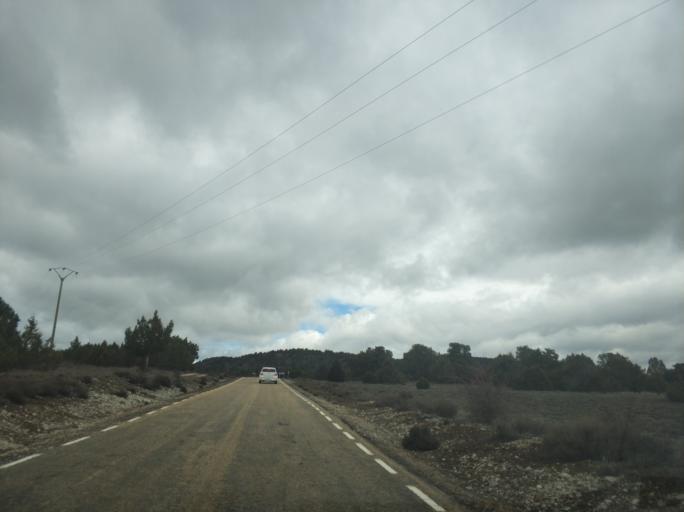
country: ES
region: Castille and Leon
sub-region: Provincia de Soria
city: Abejar
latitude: 41.7854
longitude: -2.7704
